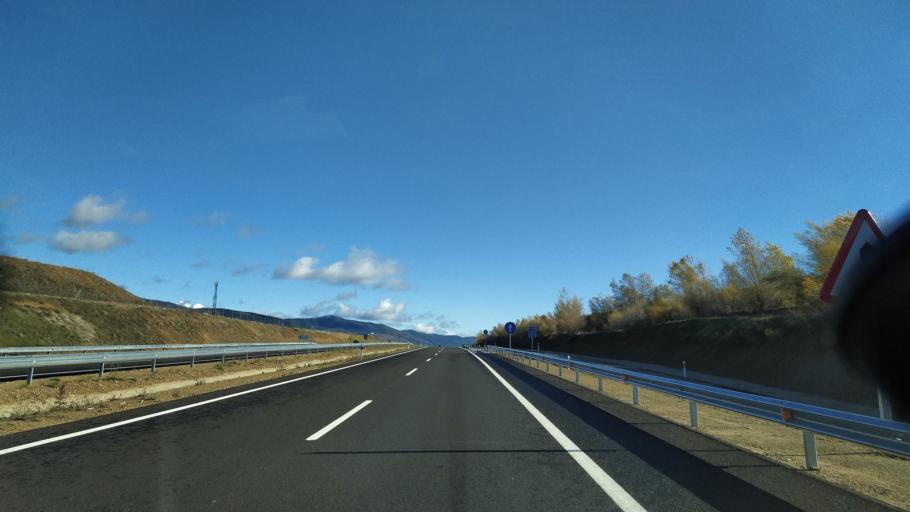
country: ES
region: Aragon
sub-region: Provincia de Huesca
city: Santa Cruz de la Seros
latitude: 42.5619
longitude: -0.6499
